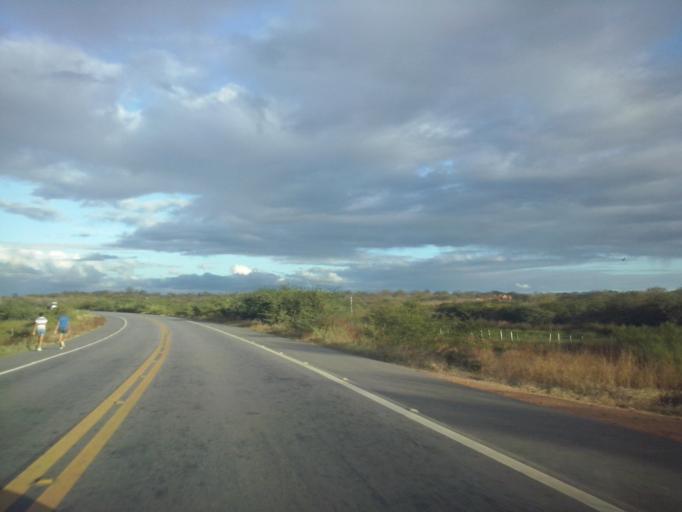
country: BR
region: Paraiba
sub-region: Patos
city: Patos
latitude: -6.9454
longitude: -37.4038
